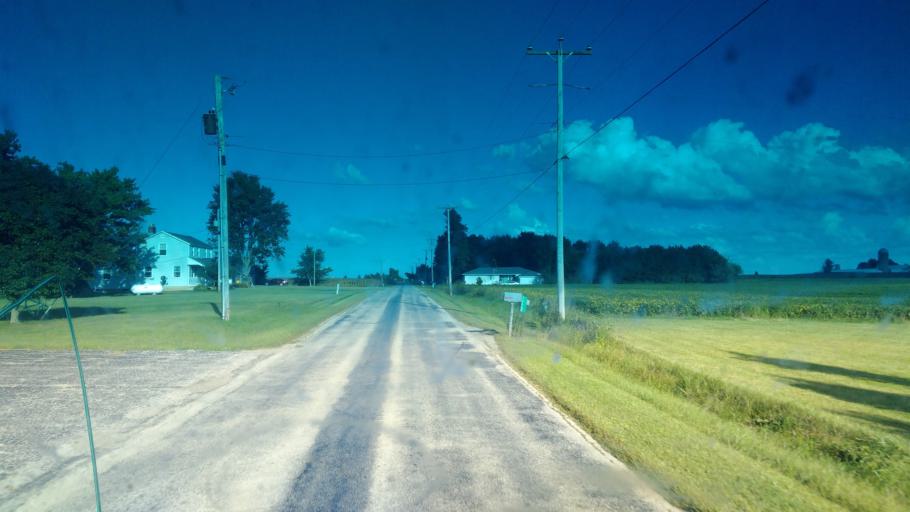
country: US
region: Ohio
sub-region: Hancock County
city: Arlington
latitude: 40.9356
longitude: -83.6205
